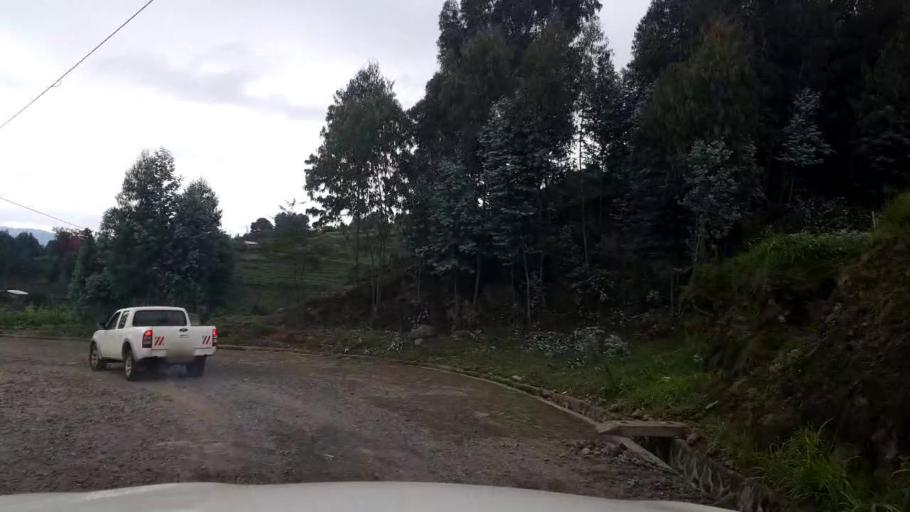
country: RW
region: Northern Province
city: Musanze
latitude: -1.4966
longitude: 29.5330
